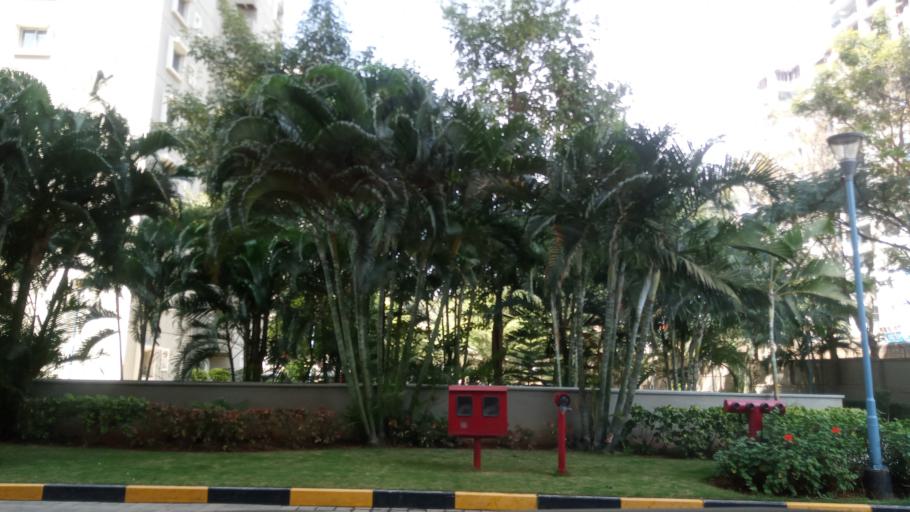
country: IN
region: Karnataka
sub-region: Bangalore Urban
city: Yelahanka
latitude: 13.0456
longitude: 77.5018
